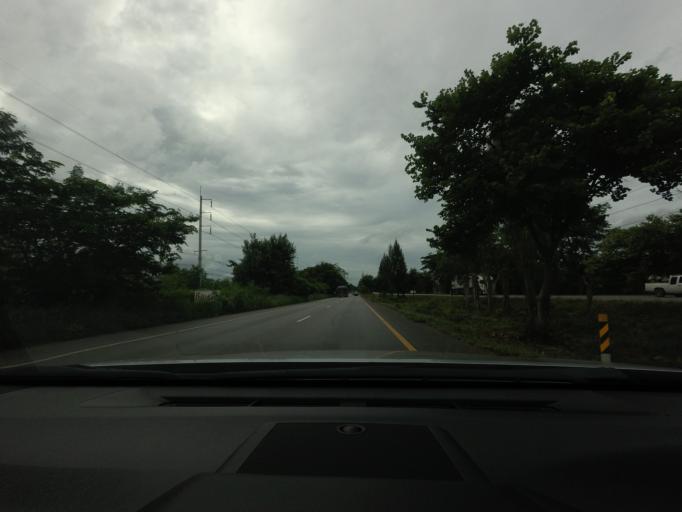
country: TH
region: Prachuap Khiri Khan
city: Hua Hin
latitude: 12.6127
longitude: 99.8603
